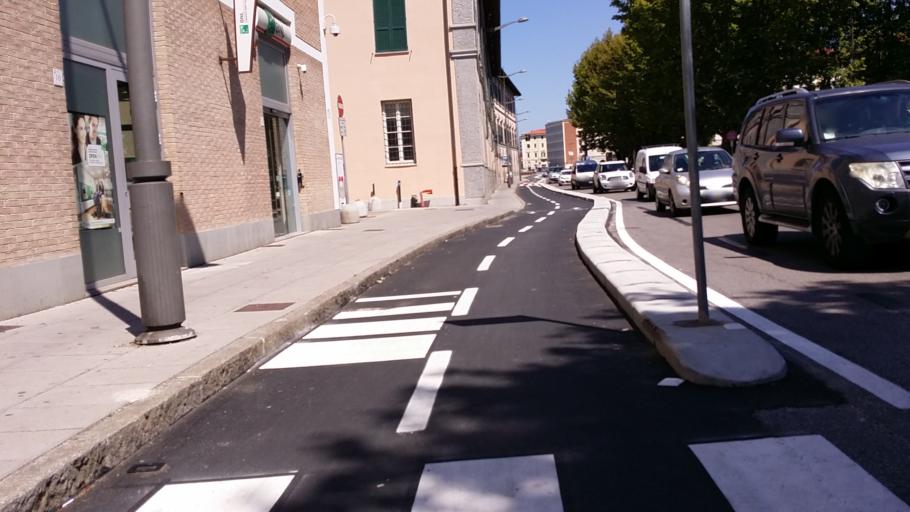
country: IT
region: Tuscany
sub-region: Provincia di Livorno
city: Livorno
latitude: 43.5437
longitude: 10.3038
